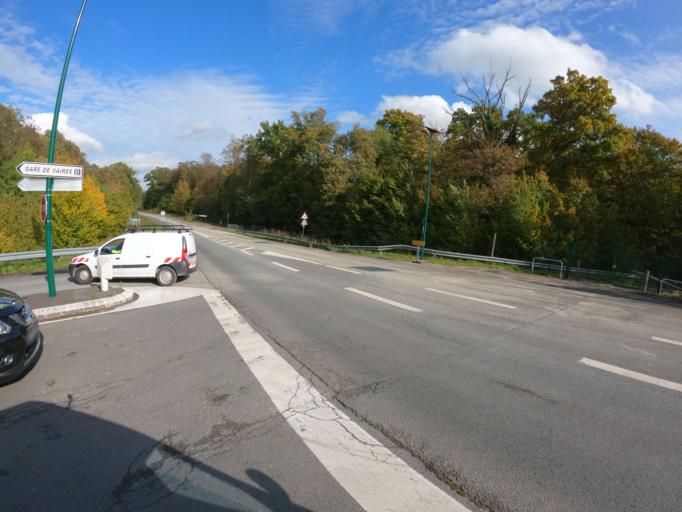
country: FR
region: Ile-de-France
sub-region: Departement de Seine-et-Marne
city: Vaires-sur-Marne
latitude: 48.8766
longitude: 2.6492
